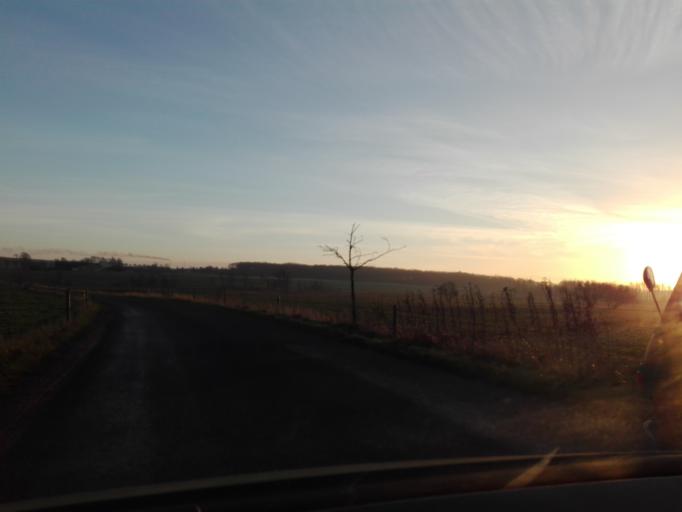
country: DK
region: Central Jutland
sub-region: Skanderborg Kommune
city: Galten
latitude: 56.1711
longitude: 9.9268
